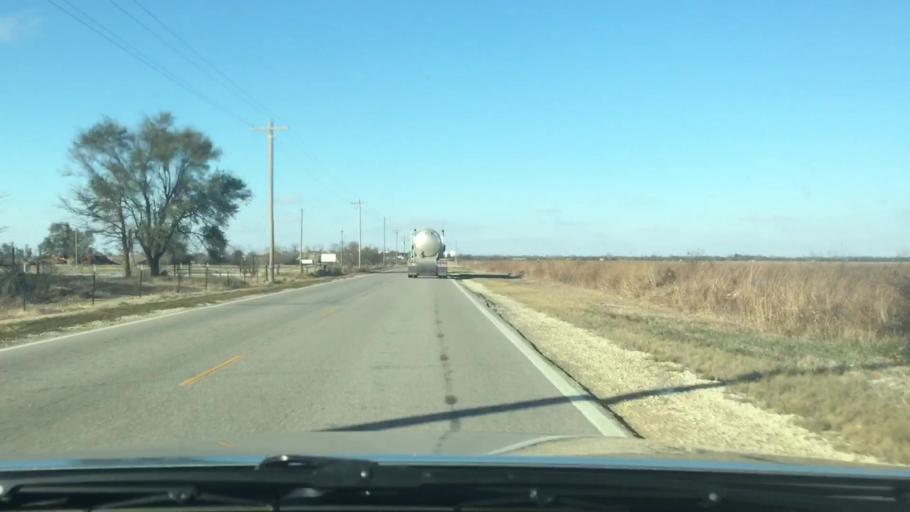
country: US
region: Kansas
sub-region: Rice County
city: Sterling
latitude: 38.1743
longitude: -98.2068
